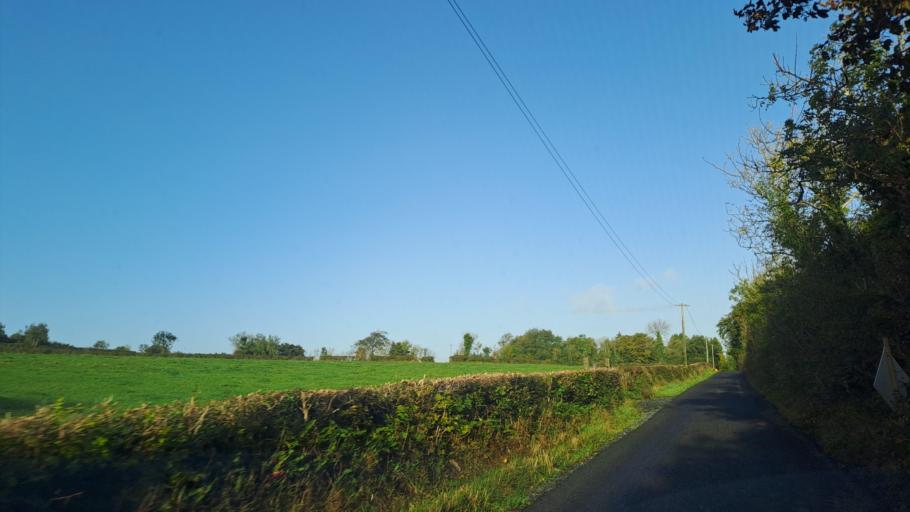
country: IE
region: Ulster
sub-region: County Monaghan
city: Castleblayney
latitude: 54.0881
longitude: -6.8665
